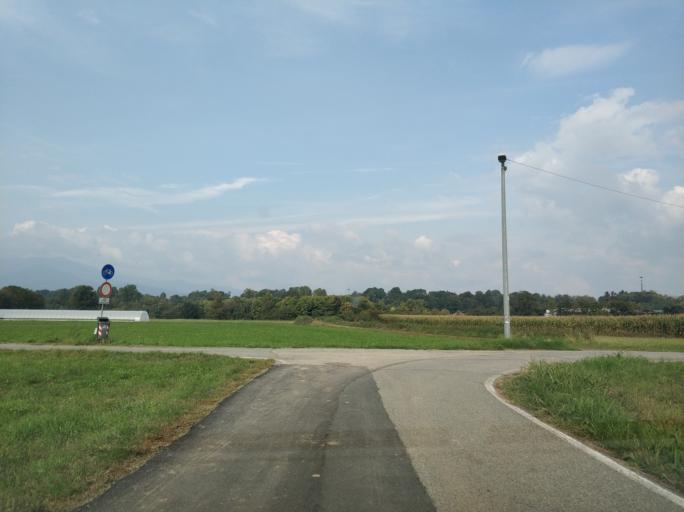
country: IT
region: Piedmont
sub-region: Provincia di Torino
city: San Carlo Canavese
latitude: 45.2416
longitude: 7.5955
